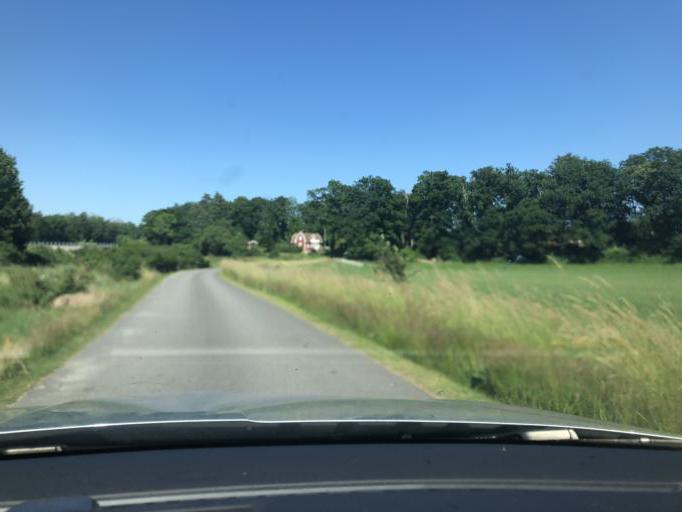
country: SE
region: Blekinge
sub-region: Karlshamns Kommun
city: Morrum
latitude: 56.1728
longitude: 14.7106
